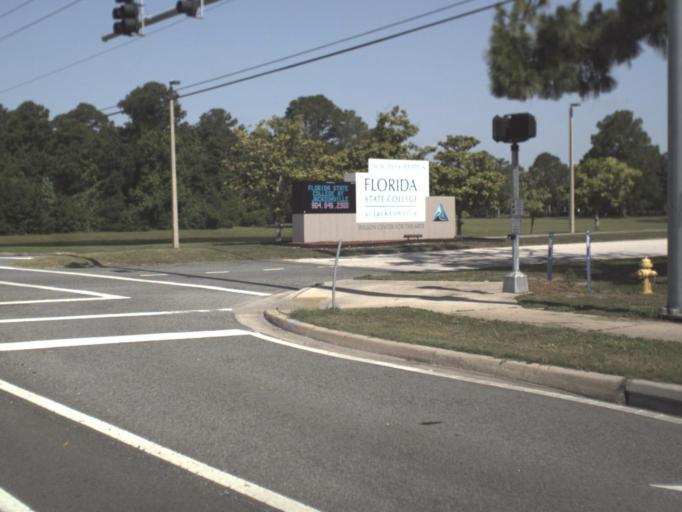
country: US
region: Florida
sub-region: Duval County
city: Neptune Beach
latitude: 30.2872
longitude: -81.5101
